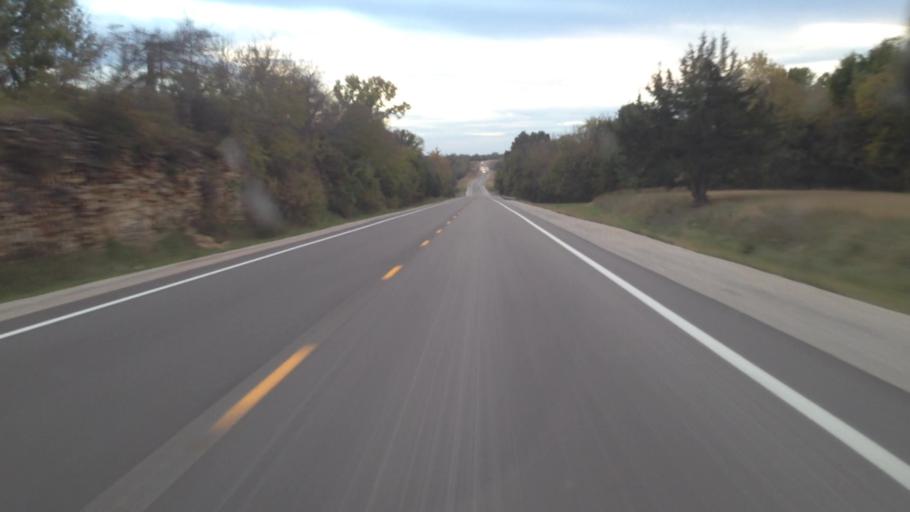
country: US
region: Kansas
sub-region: Anderson County
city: Garnett
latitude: 38.3471
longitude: -95.2488
